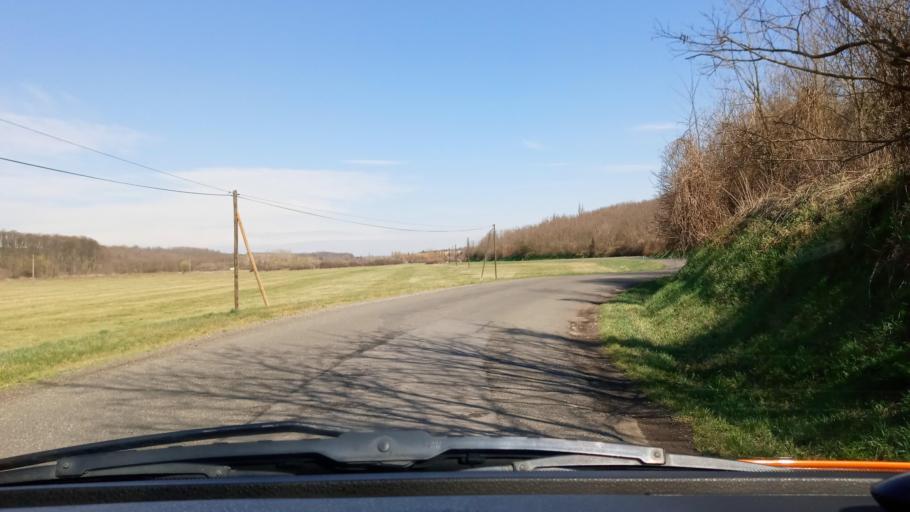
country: HU
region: Baranya
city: Pecsvarad
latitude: 46.0616
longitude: 18.4590
